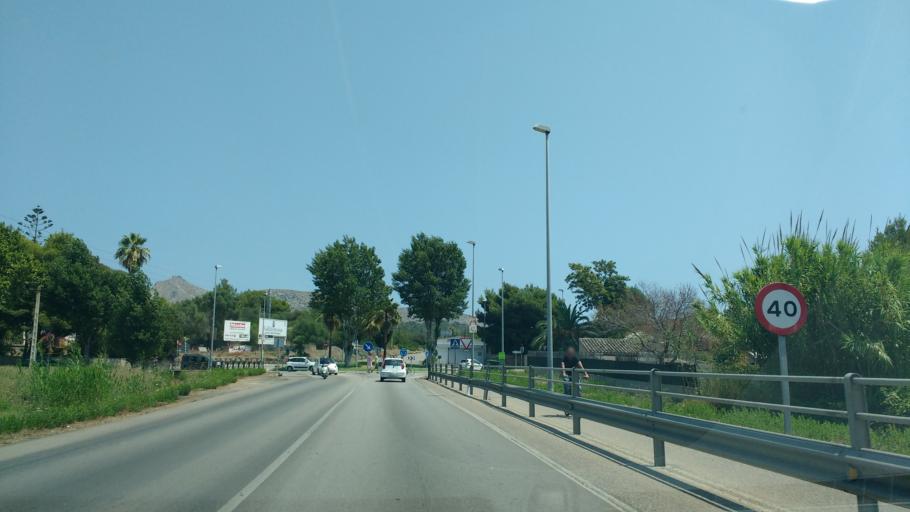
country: ES
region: Balearic Islands
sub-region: Illes Balears
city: Port d'Alcudia
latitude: 39.8459
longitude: 3.1300
